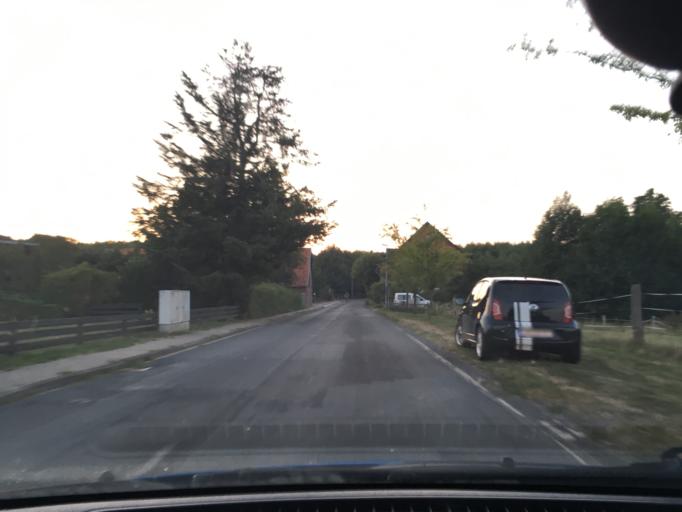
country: DE
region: Lower Saxony
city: Barnstedt
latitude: 53.1391
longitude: 10.3721
